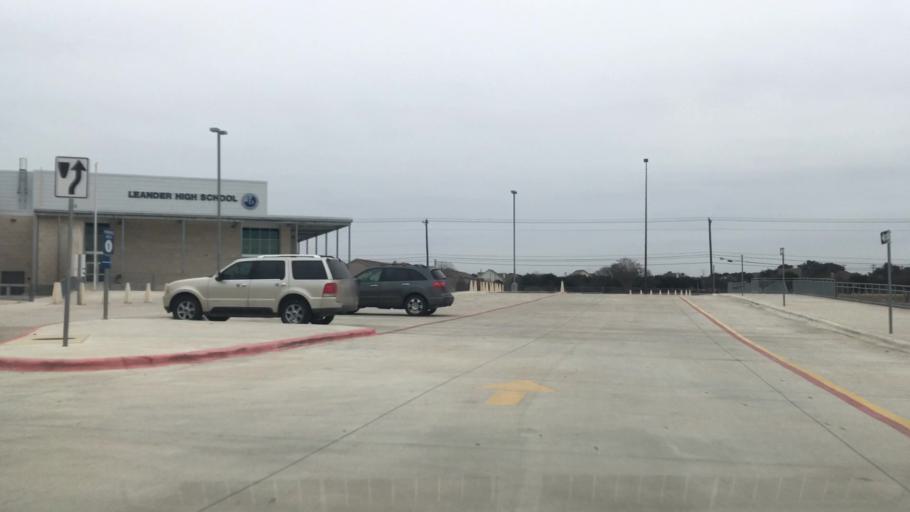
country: US
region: Texas
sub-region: Williamson County
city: Leander
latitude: 30.5380
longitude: -97.8497
